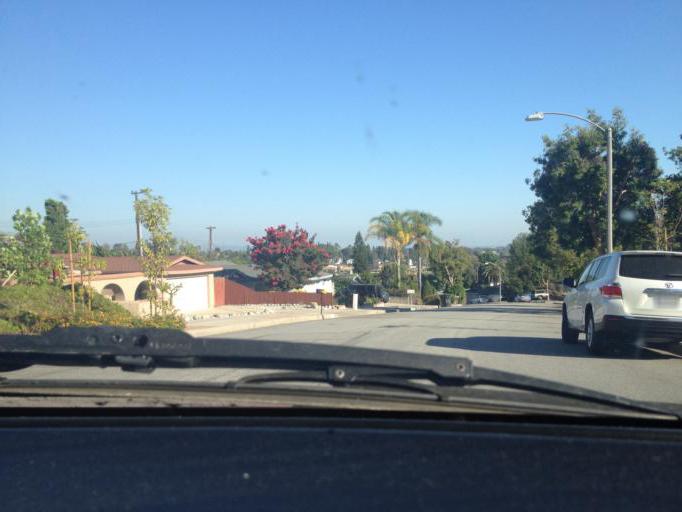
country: US
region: California
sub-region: Orange County
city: Brea
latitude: 33.9375
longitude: -117.8973
